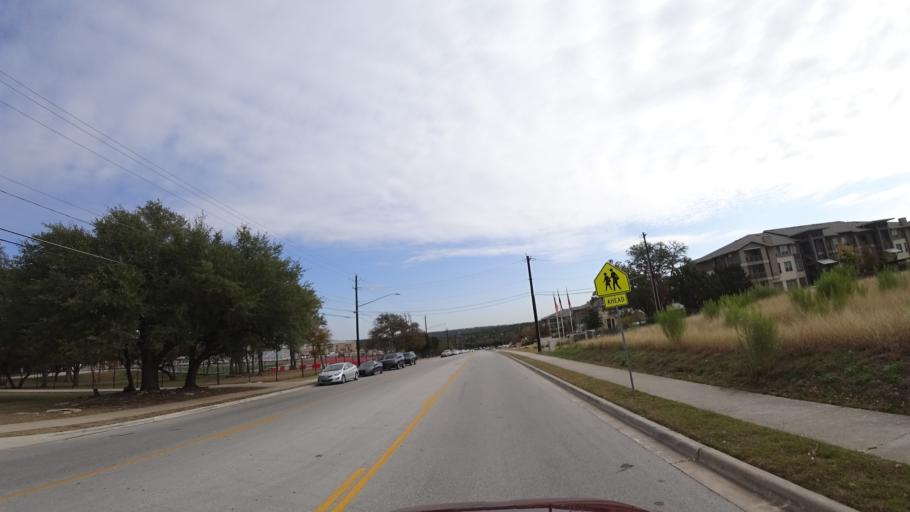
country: US
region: Texas
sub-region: Williamson County
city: Anderson Mill
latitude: 30.3953
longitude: -97.8290
